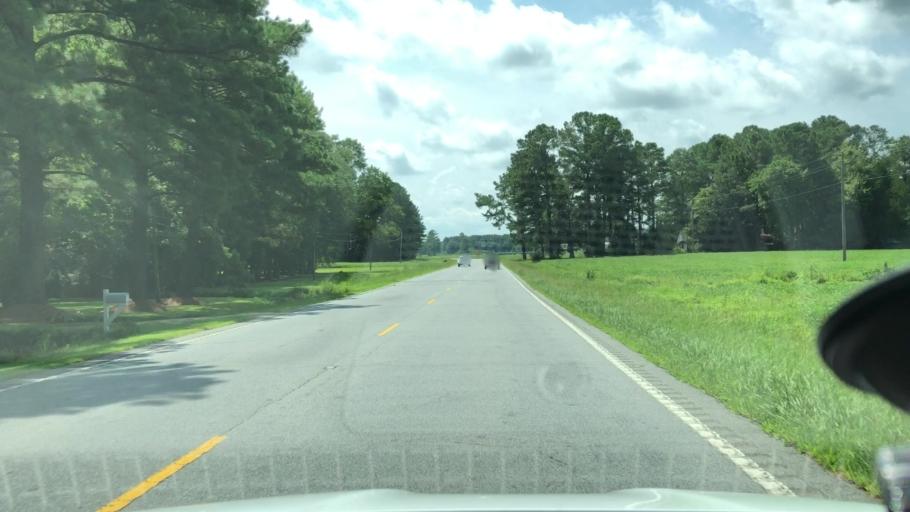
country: US
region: North Carolina
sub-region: Beaufort County
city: Washington
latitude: 35.6561
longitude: -77.0719
